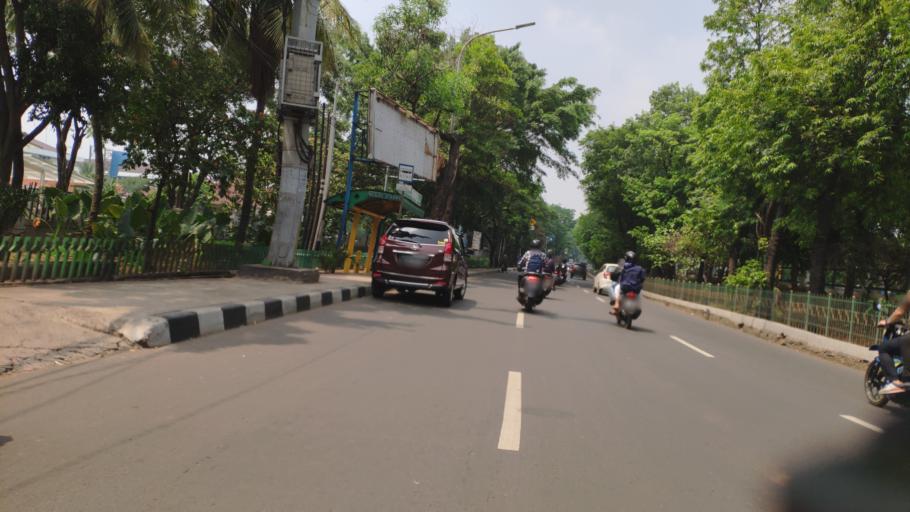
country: ID
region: West Java
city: Depok
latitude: -6.3424
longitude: 106.8333
